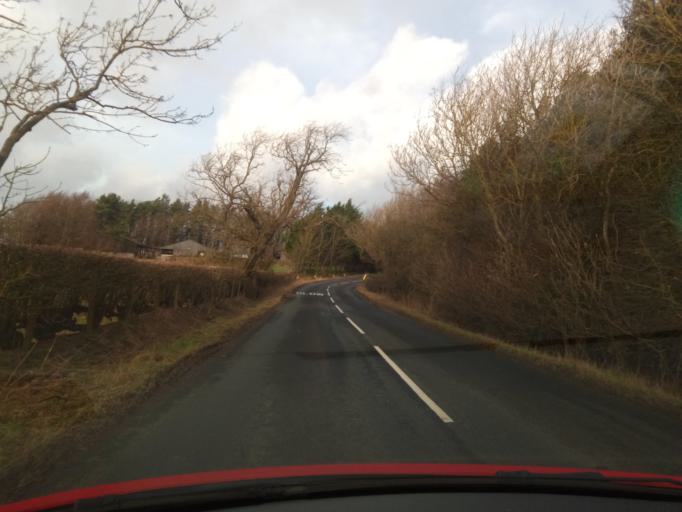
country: GB
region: England
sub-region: Northumberland
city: Rothley
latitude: 55.1092
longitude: -2.0092
